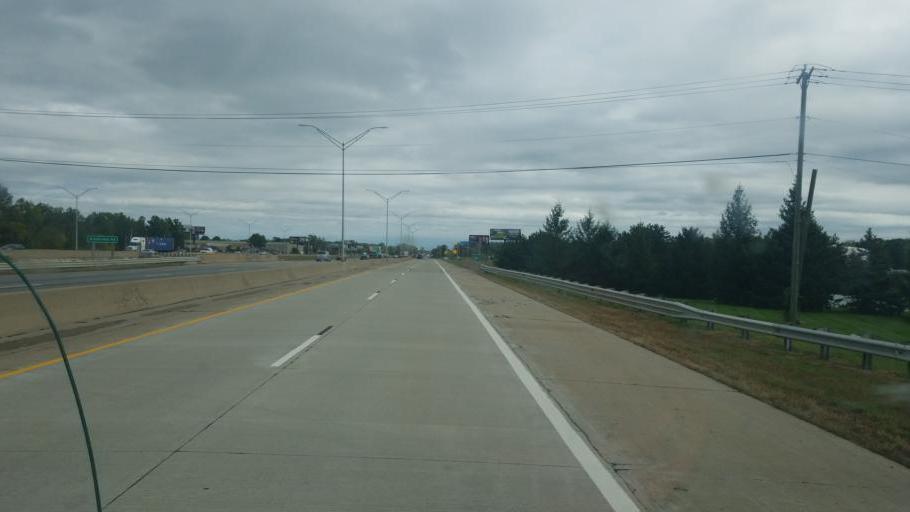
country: US
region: Michigan
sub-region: Wayne County
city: Inkster
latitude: 42.2417
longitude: -83.3292
